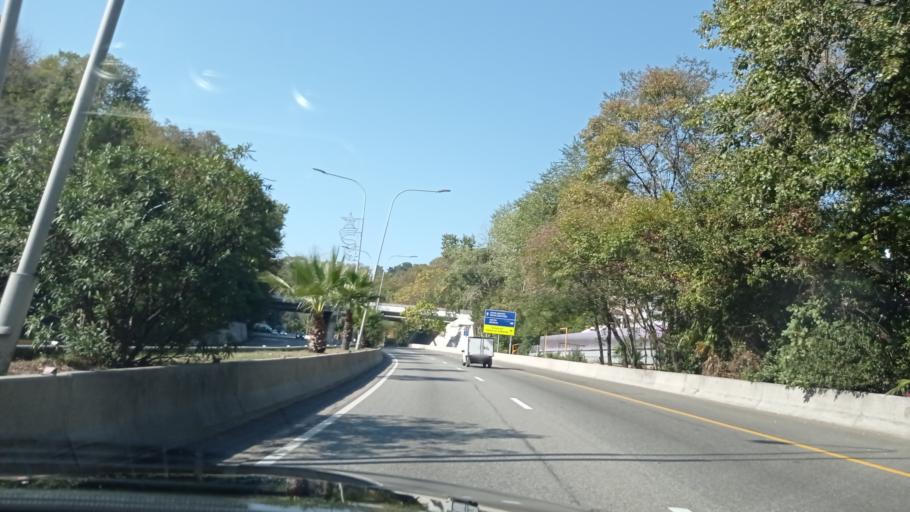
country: RU
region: Krasnodarskiy
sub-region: Sochi City
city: Khosta
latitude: 43.5176
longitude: 39.8557
